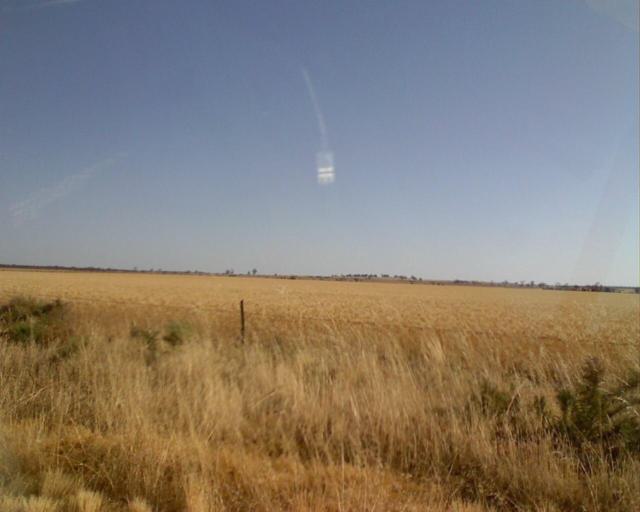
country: AU
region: Western Australia
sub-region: Wongan-Ballidu
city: Wongan Hills
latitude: -30.0388
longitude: 116.8175
